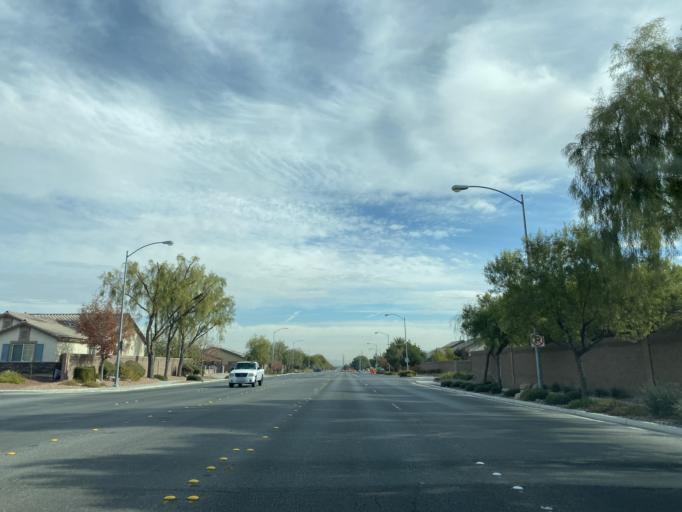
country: US
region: Nevada
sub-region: Clark County
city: North Las Vegas
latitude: 36.2469
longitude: -115.1381
